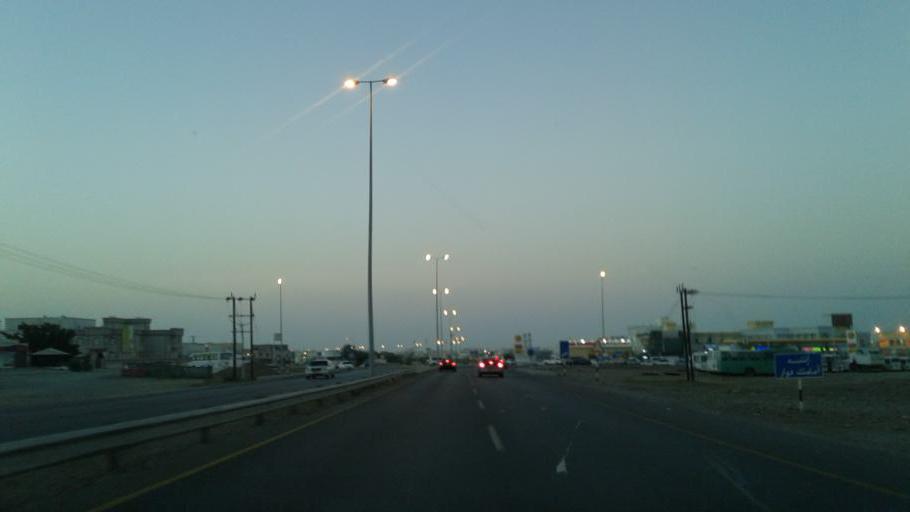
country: OM
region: Muhafazat Masqat
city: As Sib al Jadidah
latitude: 23.6001
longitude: 58.2174
